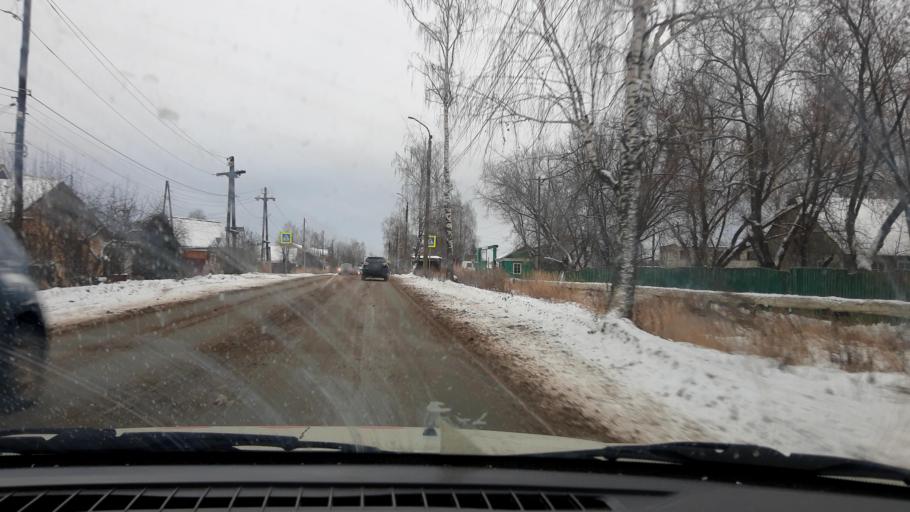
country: RU
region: Nizjnij Novgorod
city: Gorodets
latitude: 56.6513
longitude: 43.4897
